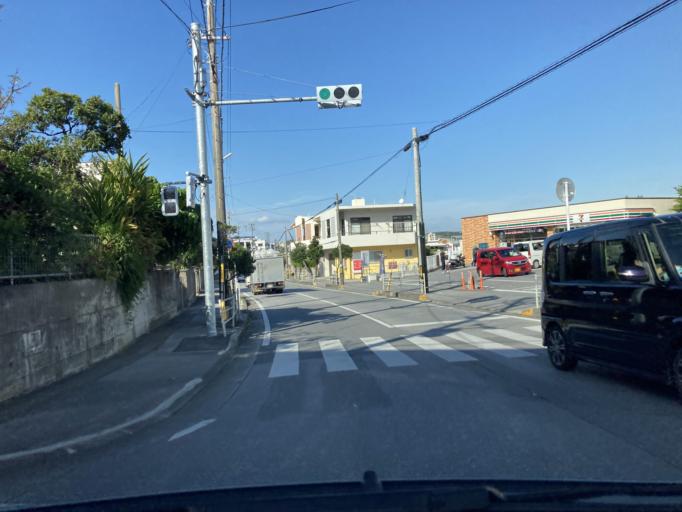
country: JP
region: Okinawa
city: Tomigusuku
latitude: 26.1801
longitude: 127.7069
